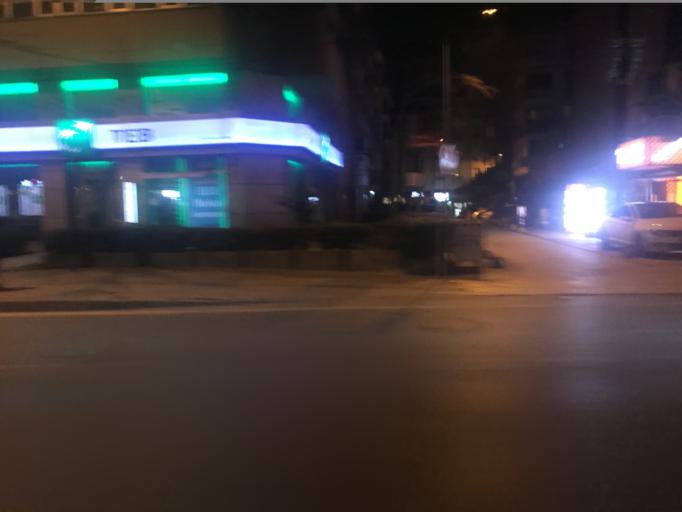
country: TR
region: Istanbul
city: Bahcelievler
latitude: 40.9834
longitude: 28.8725
